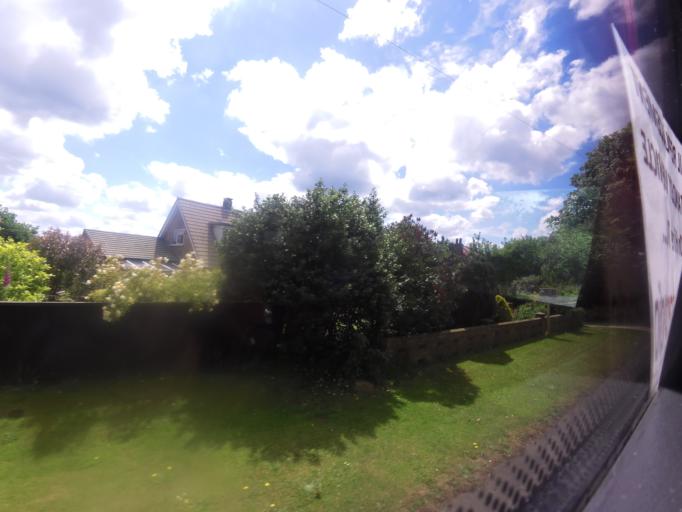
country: GB
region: England
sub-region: Norfolk
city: Cromer
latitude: 52.9206
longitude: 1.2751
